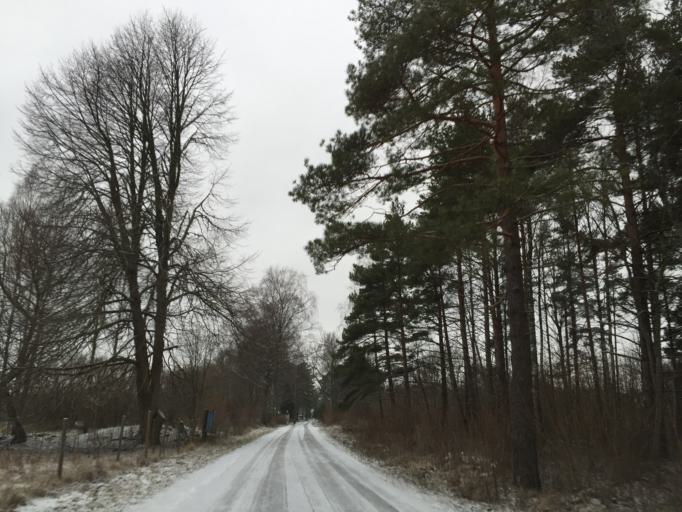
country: EE
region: Saare
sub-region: Orissaare vald
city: Orissaare
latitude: 58.6195
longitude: 23.1837
